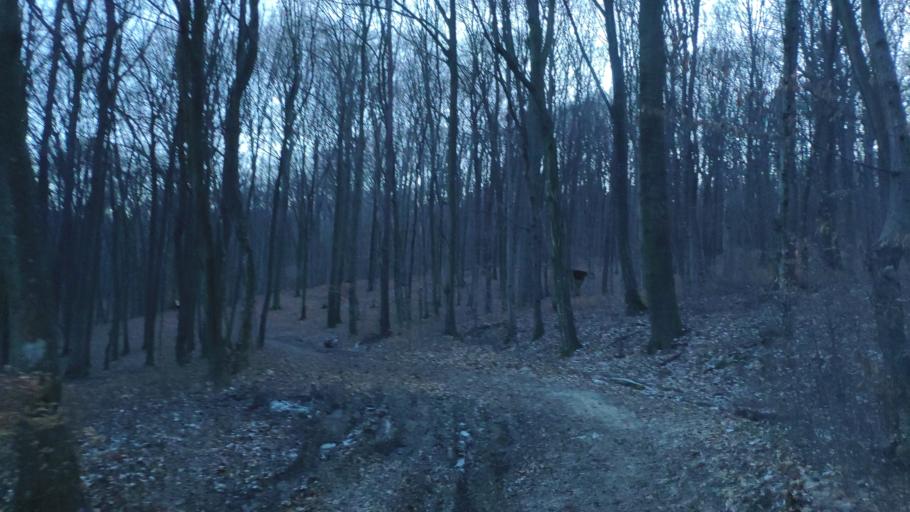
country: SK
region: Kosicky
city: Kosice
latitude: 48.8437
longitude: 21.2457
